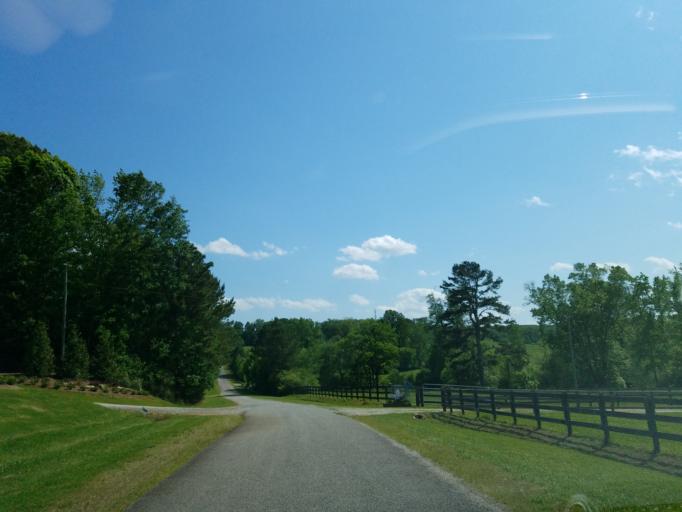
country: US
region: Georgia
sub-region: Cherokee County
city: Ball Ground
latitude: 34.2783
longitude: -84.3121
